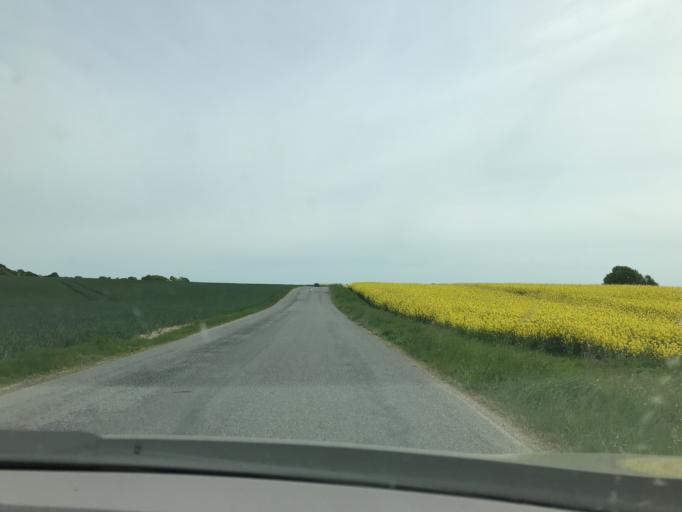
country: DK
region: Central Jutland
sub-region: Norddjurs Kommune
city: Allingabro
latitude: 56.5675
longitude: 10.2999
